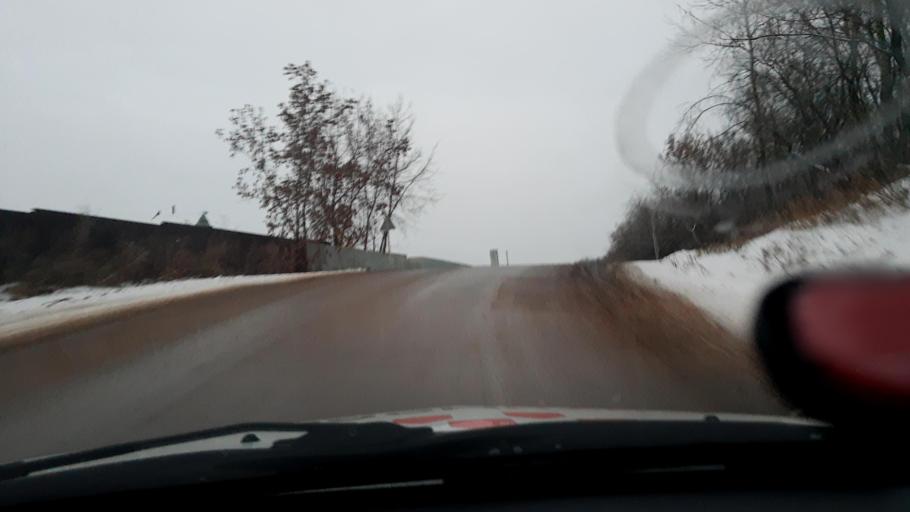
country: RU
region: Bashkortostan
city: Iglino
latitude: 54.8404
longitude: 56.4499
